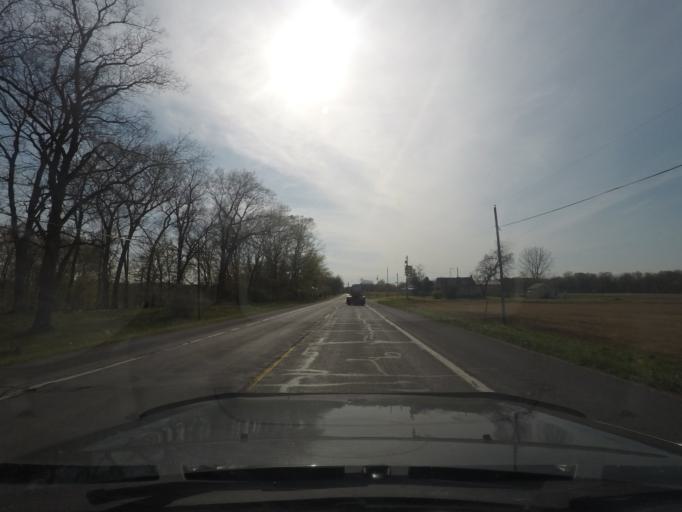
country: US
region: Indiana
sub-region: Saint Joseph County
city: New Carlisle
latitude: 41.7980
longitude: -86.4735
